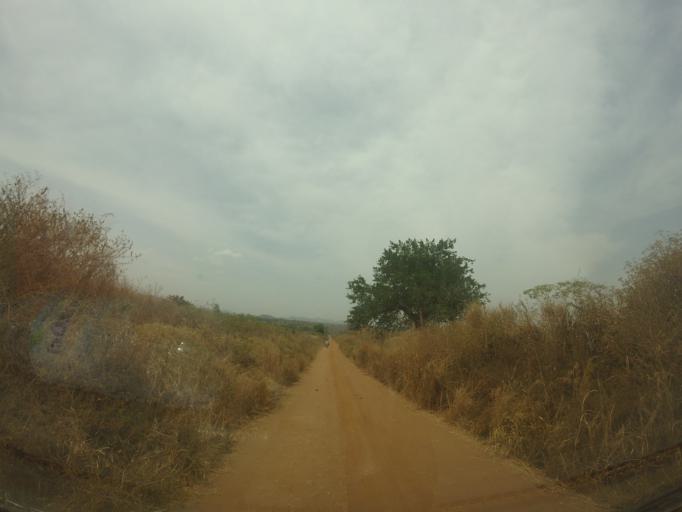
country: UG
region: Northern Region
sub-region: Nebbi District
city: Nebbi
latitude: 2.6223
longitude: 31.0408
